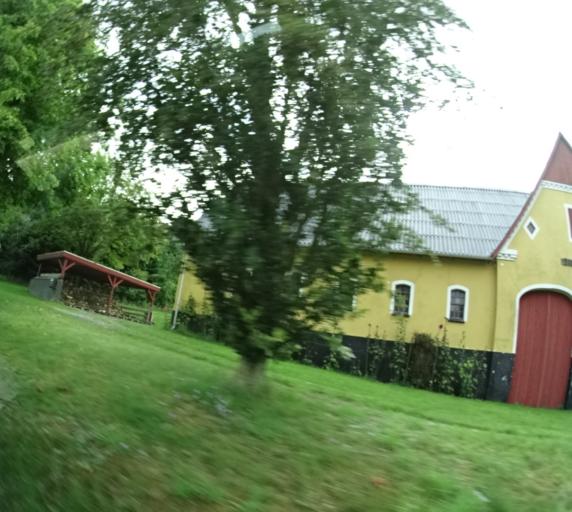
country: DK
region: Central Jutland
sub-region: Syddjurs Kommune
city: Ryomgard
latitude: 56.3928
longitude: 10.4790
